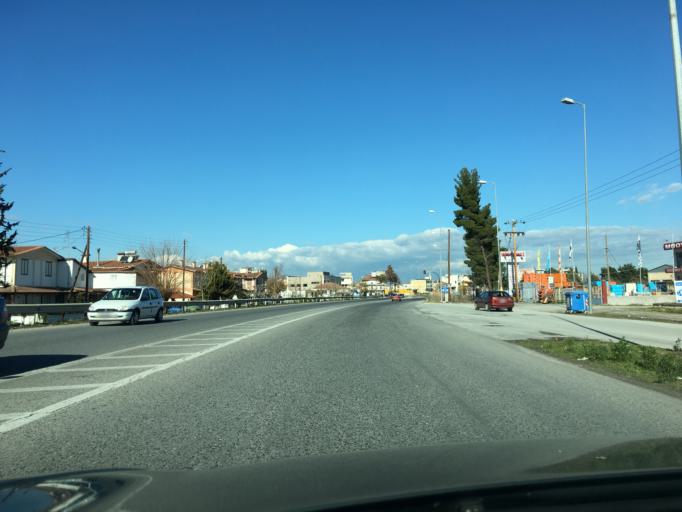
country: GR
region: Thessaly
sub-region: Nomos Larisis
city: Larisa
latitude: 39.6182
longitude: 22.4299
